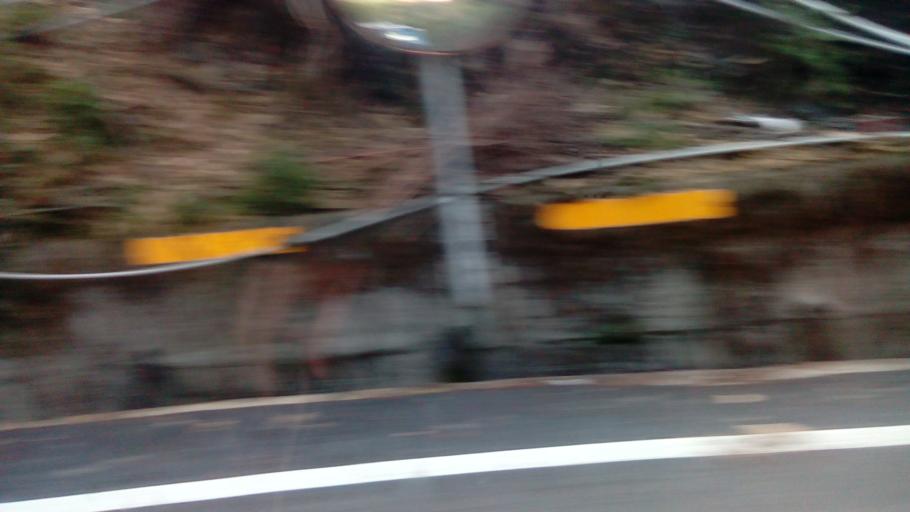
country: TW
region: Taiwan
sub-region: Hualien
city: Hualian
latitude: 24.3242
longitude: 121.3038
